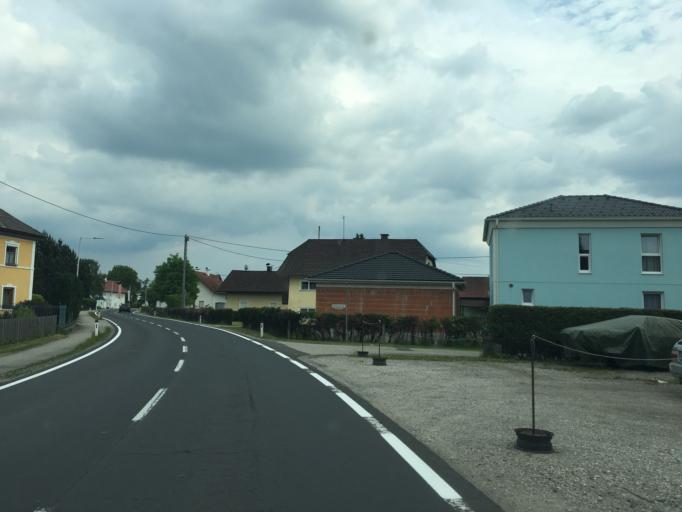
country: AT
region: Upper Austria
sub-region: Politischer Bezirk Braunau am Inn
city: Braunau am Inn
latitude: 48.1509
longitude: 13.1214
